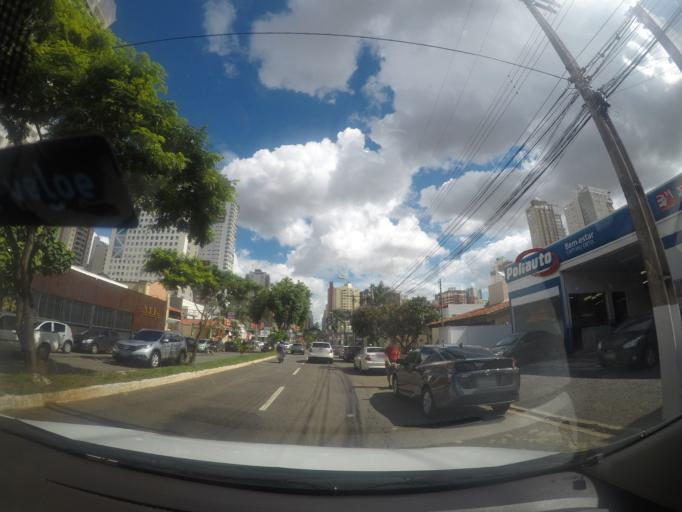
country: BR
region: Goias
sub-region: Goiania
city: Goiania
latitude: -16.7085
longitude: -49.2672
